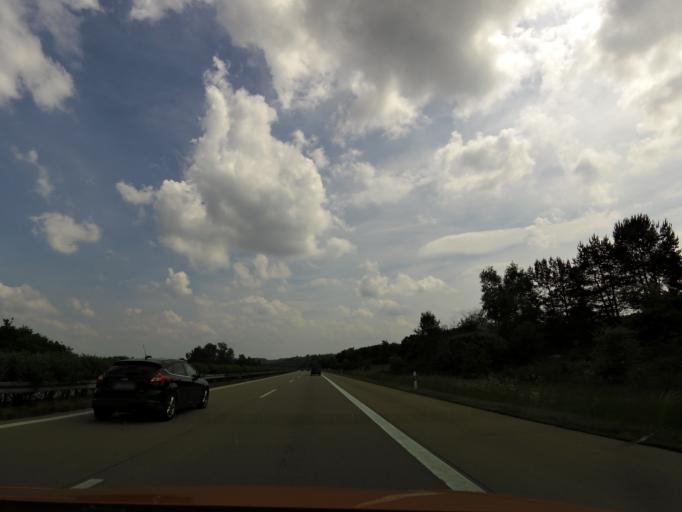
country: DE
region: Mecklenburg-Vorpommern
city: Siggelkow
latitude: 53.3144
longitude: 11.9008
